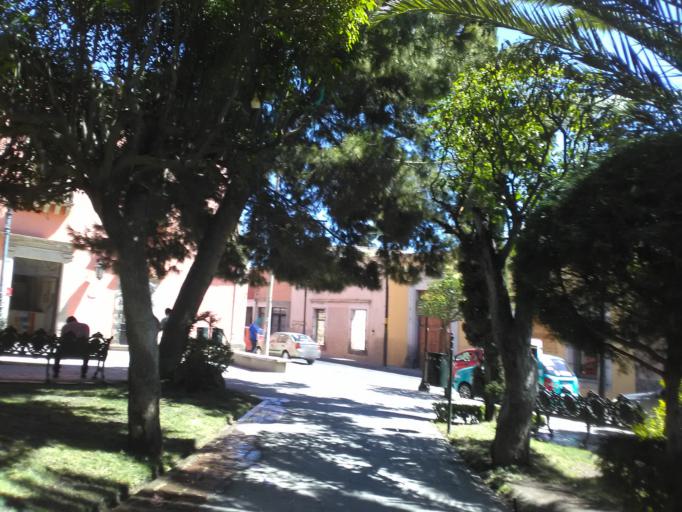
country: MX
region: Durango
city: Victoria de Durango
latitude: 24.0301
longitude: -104.6707
